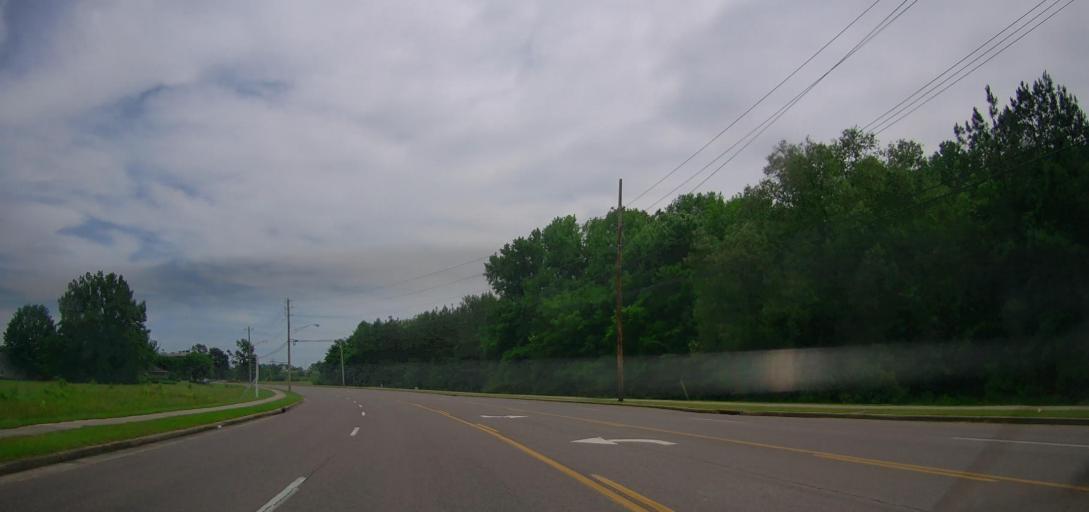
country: US
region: Tennessee
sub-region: Shelby County
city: Germantown
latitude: 35.0723
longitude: -89.8491
